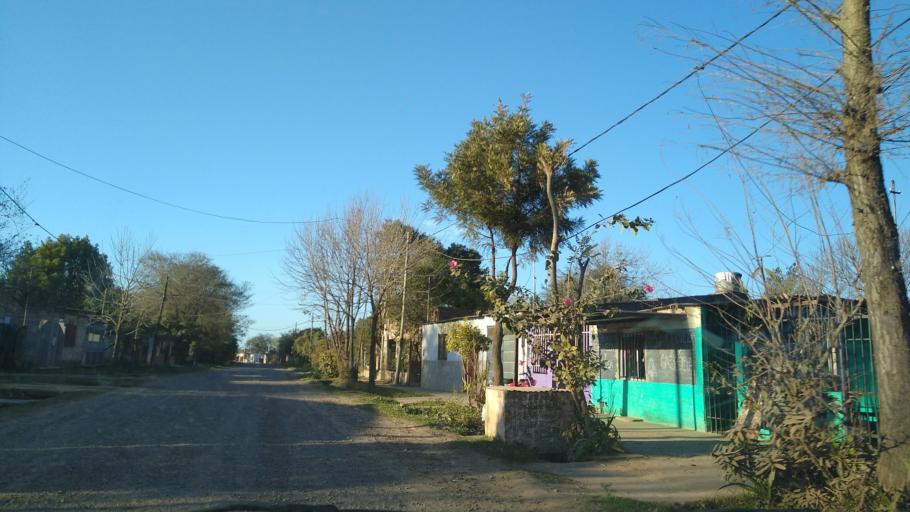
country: AR
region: Chaco
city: Barranqueras
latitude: -27.4728
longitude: -58.9477
